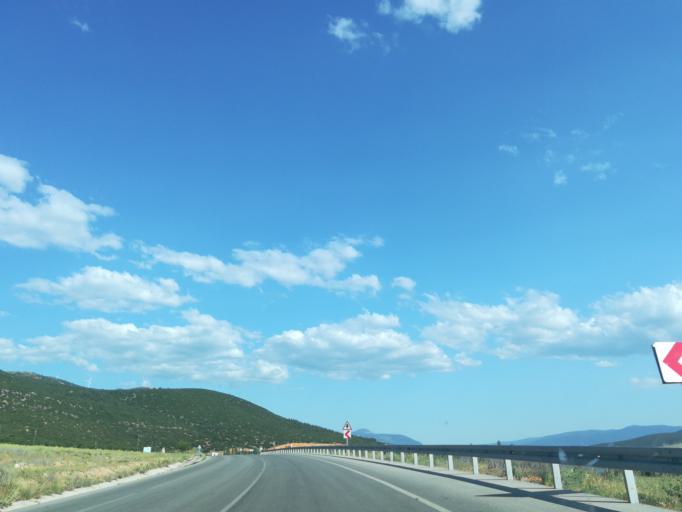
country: TR
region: Denizli
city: Ishakli
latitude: 38.1657
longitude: 30.0733
